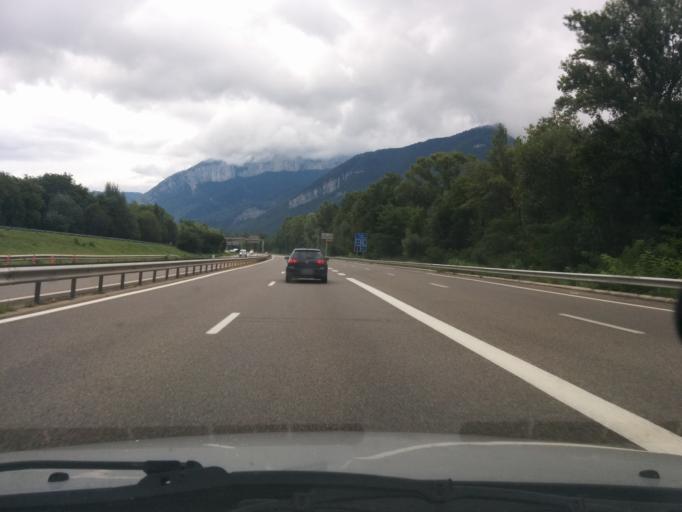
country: FR
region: Rhone-Alpes
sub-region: Departement de l'Isere
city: Voreppe
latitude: 45.2941
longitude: 5.6203
